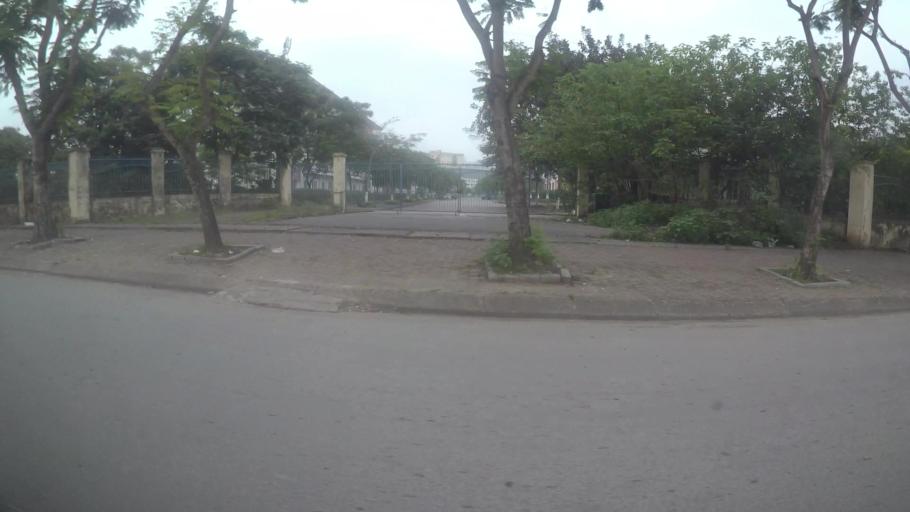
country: VN
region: Ha Noi
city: Cau Dien
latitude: 21.0250
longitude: 105.7635
